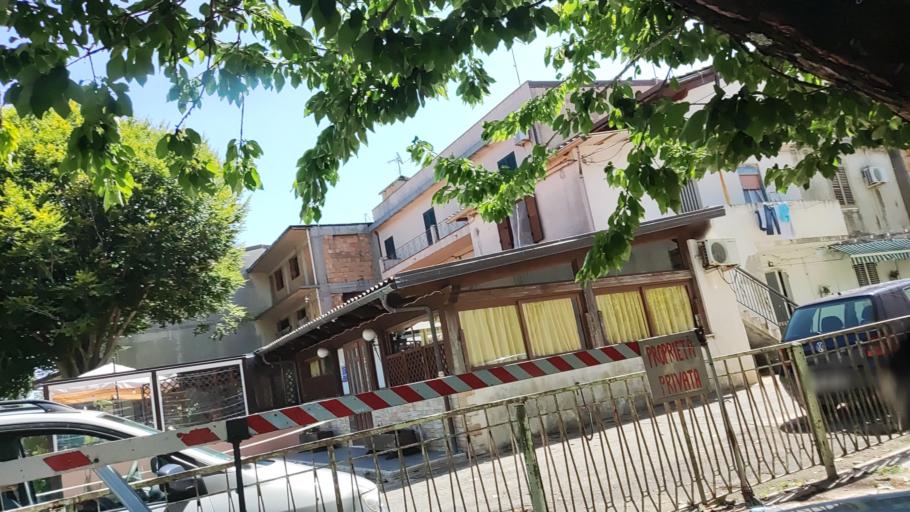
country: IT
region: Calabria
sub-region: Provincia di Reggio Calabria
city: Seminara
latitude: 38.3337
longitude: 15.8480
